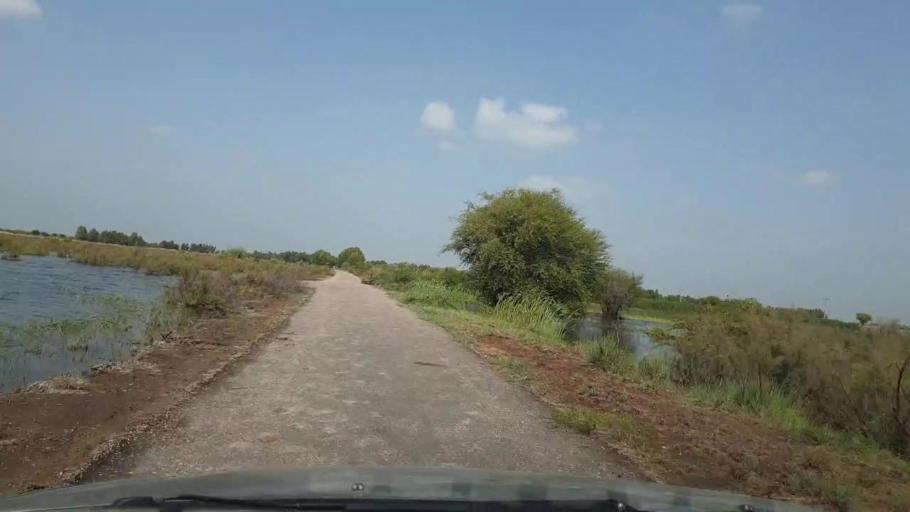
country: PK
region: Sindh
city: Rajo Khanani
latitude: 25.0318
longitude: 68.9363
